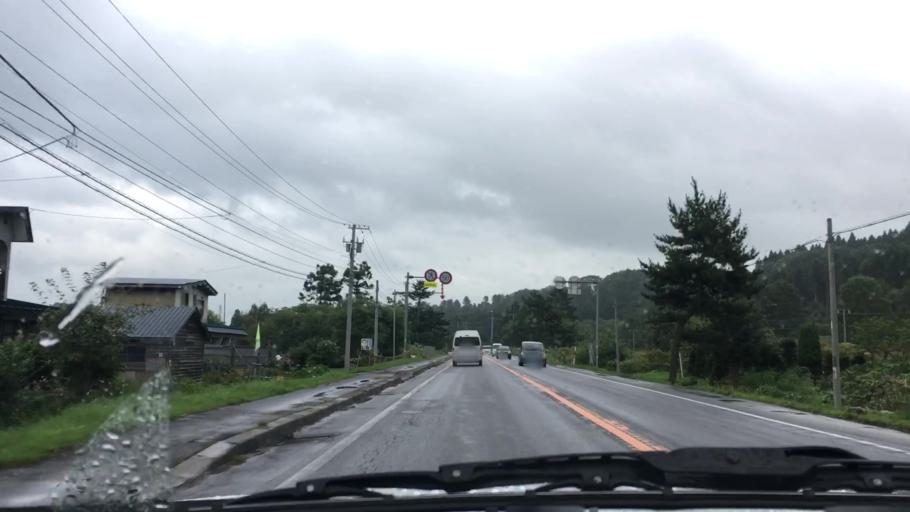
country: JP
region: Hokkaido
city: Nanae
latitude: 42.2253
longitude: 140.3438
